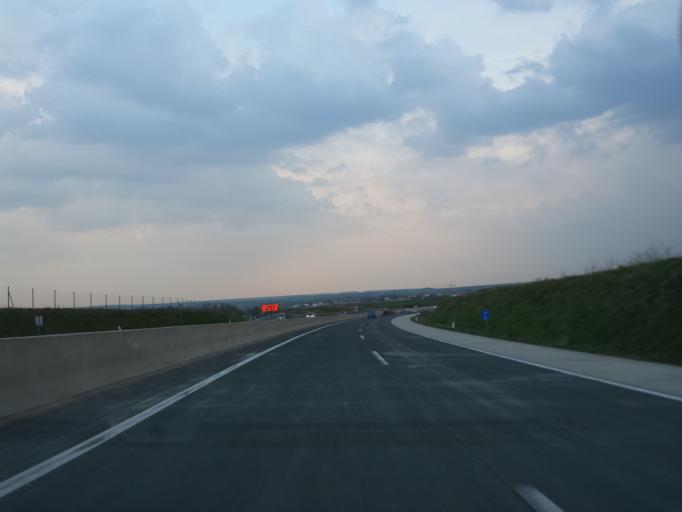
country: AT
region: Lower Austria
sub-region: Politischer Bezirk Mistelbach
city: Gaweinstal
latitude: 48.4965
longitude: 16.5986
